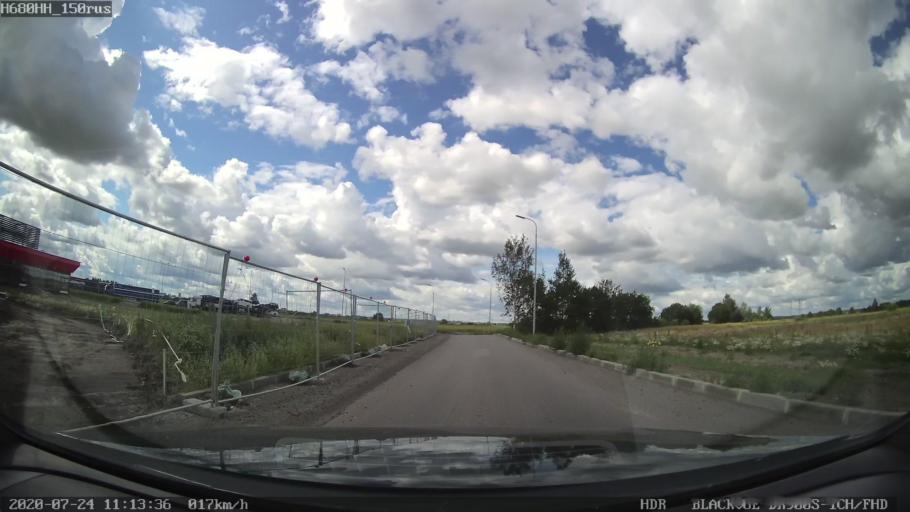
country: RU
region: Leningrad
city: Fedorovskoye
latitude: 59.7020
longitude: 30.5512
